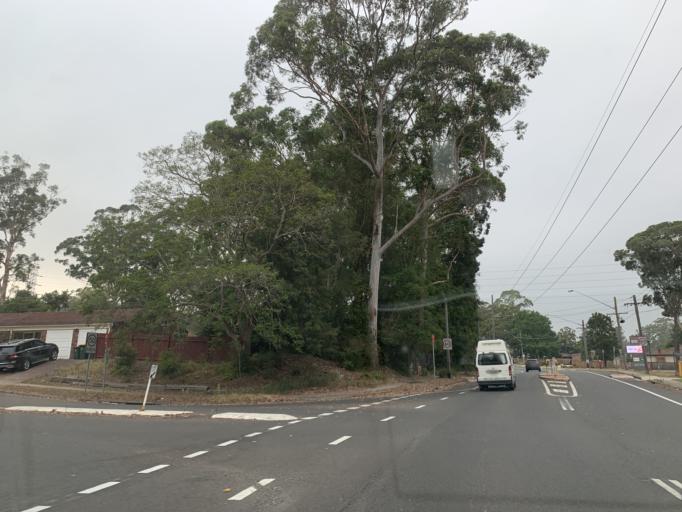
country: AU
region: New South Wales
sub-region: The Hills Shire
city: West Pennant
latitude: -33.7339
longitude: 151.0447
